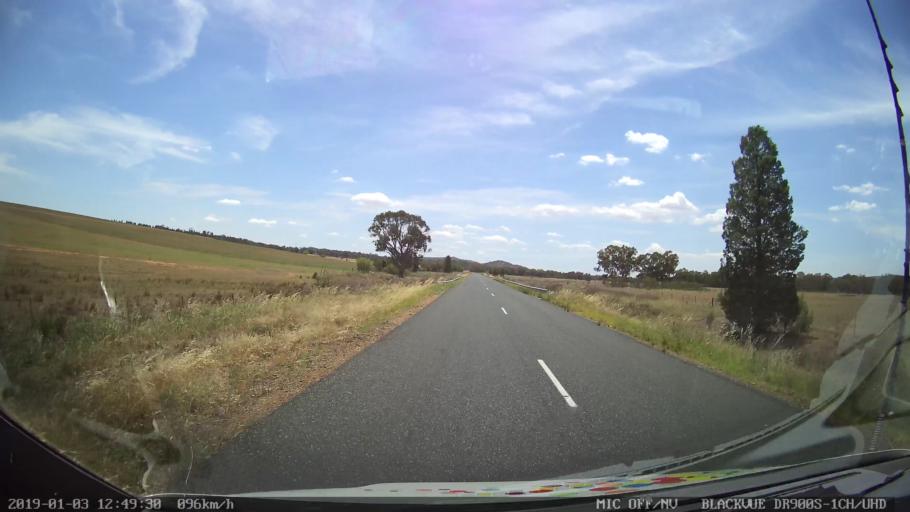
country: AU
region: New South Wales
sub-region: Weddin
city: Grenfell
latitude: -33.7028
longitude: 148.2617
